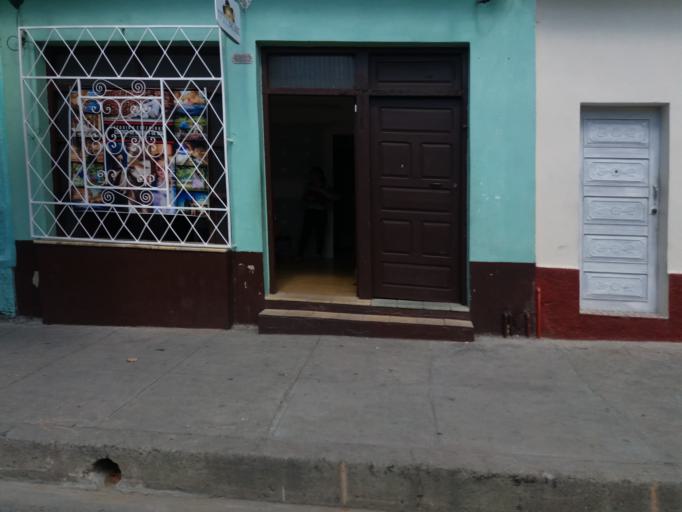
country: CU
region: Cienfuegos
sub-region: Municipio de Cienfuegos
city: Cienfuegos
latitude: 22.1469
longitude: -80.4462
